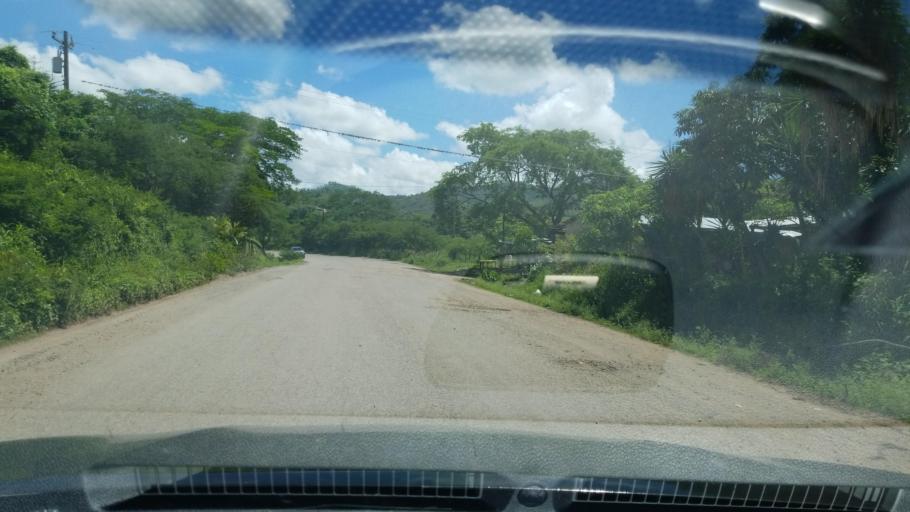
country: HN
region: Francisco Morazan
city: San Juan de Flores
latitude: 14.3098
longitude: -87.0363
